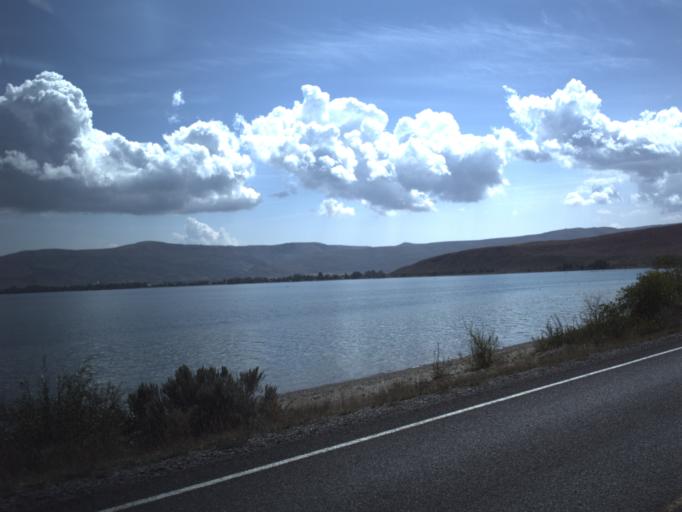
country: US
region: Utah
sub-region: Rich County
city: Randolph
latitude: 41.8643
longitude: -111.3647
